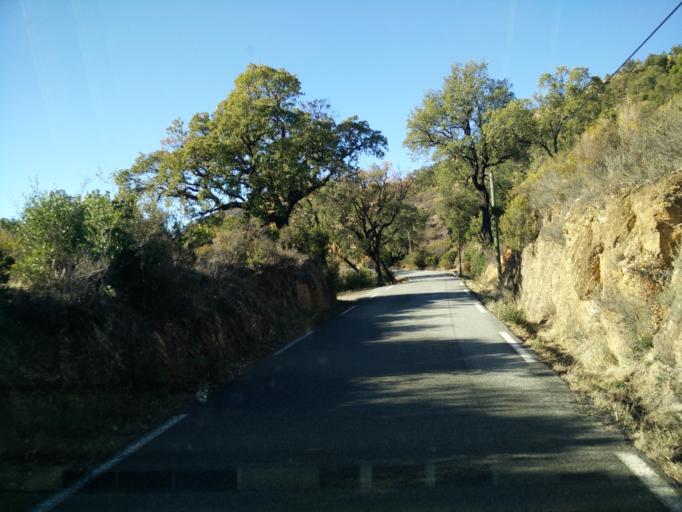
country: FR
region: Provence-Alpes-Cote d'Azur
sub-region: Departement du Var
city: La Garde-Freinet
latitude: 43.2594
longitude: 6.4542
